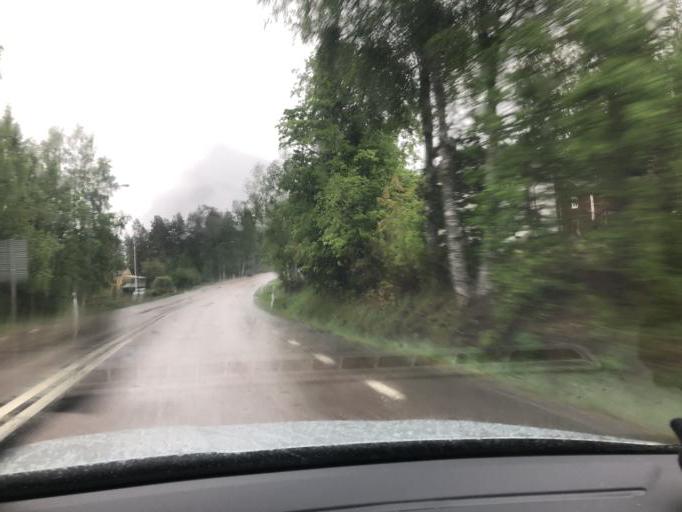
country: SE
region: Vaesternorrland
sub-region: Haernoesands Kommun
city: Haernoesand
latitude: 62.7904
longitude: 17.9150
